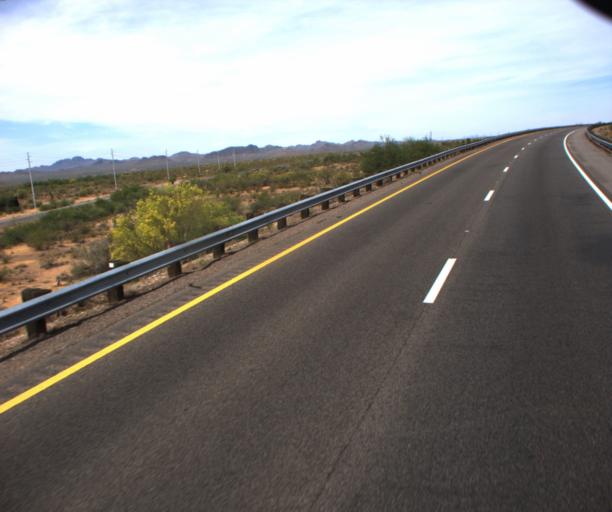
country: US
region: Arizona
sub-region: Maricopa County
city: Wickenburg
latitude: 33.8392
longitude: -112.6092
